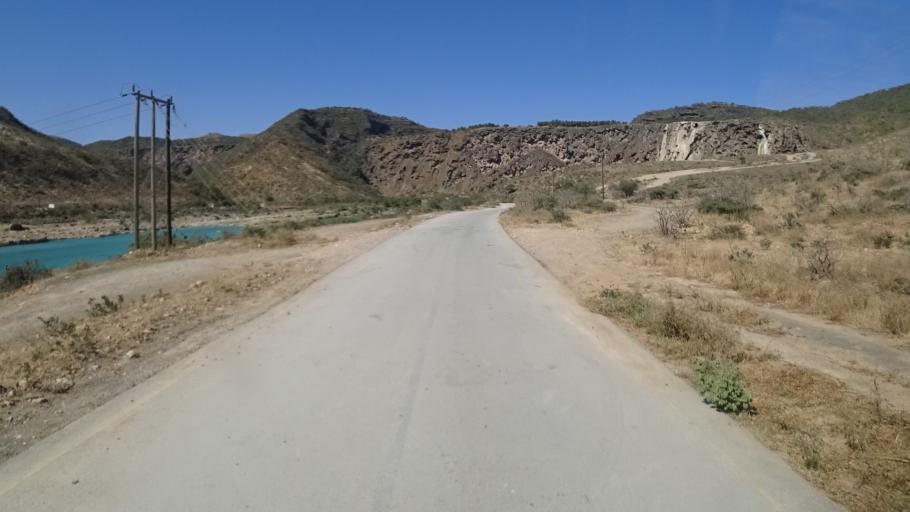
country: OM
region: Zufar
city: Salalah
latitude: 17.0704
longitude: 54.4318
